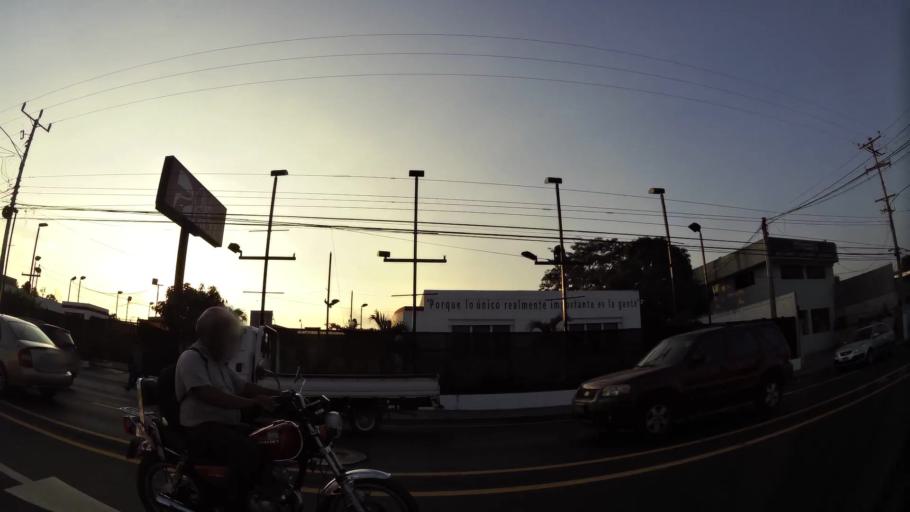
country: SV
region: San Salvador
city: San Salvador
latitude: 13.6926
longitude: -89.2169
